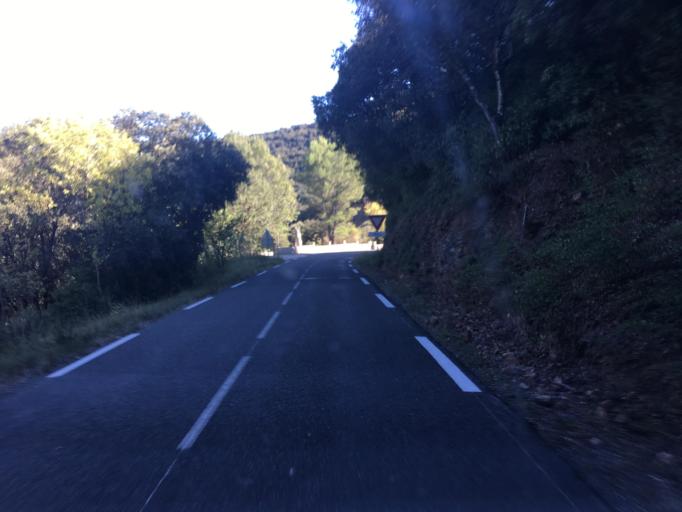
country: FR
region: Languedoc-Roussillon
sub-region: Departement de l'Herault
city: Nebian
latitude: 43.6107
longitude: 3.3823
